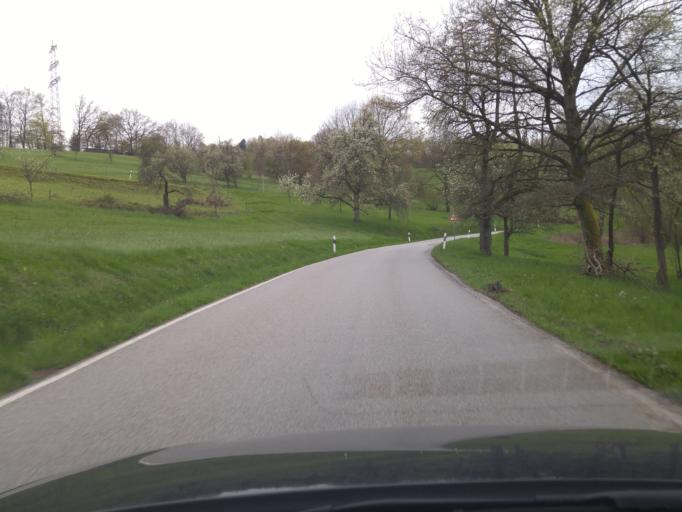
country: DE
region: Hesse
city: Neckarsteinach
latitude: 49.3863
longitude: 8.8585
